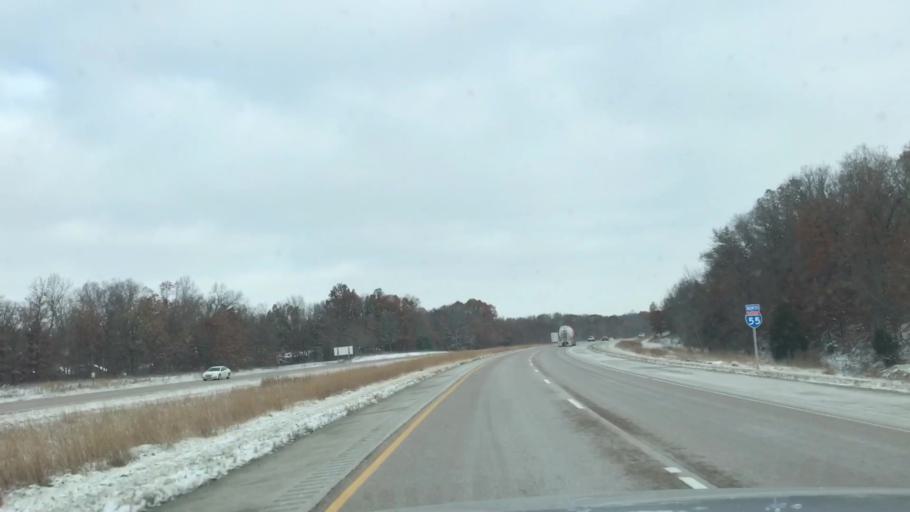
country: US
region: Illinois
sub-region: Macoupin County
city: Mount Olive
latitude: 39.0783
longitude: -89.7555
